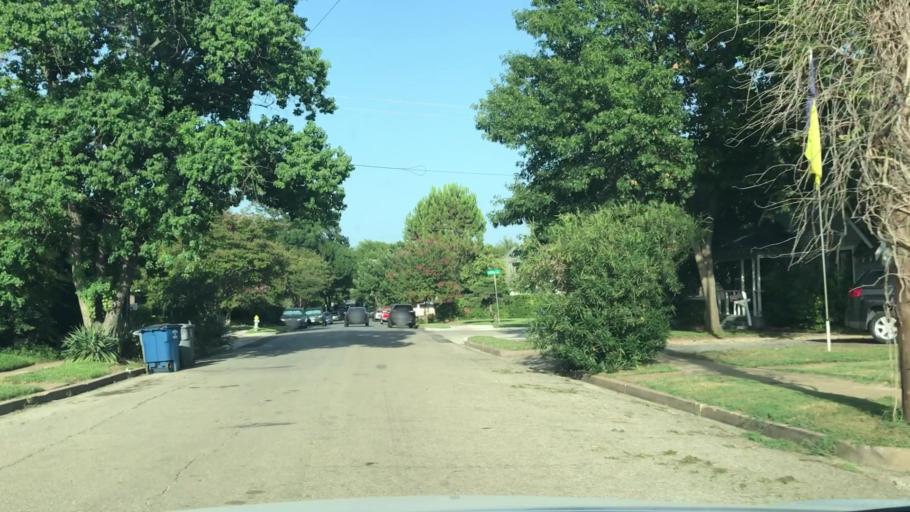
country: US
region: Texas
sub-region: Dallas County
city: Highland Park
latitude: 32.8220
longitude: -96.7642
